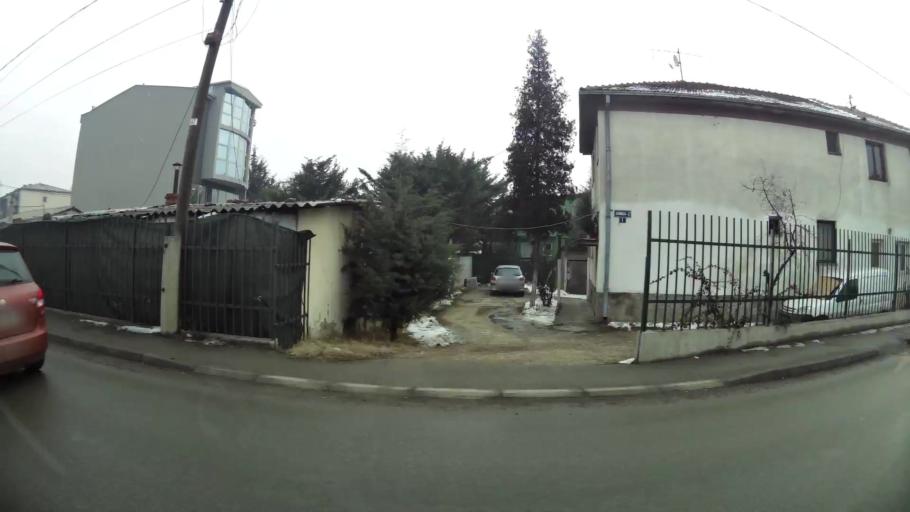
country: MK
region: Kisela Voda
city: Kisela Voda
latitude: 41.9972
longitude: 21.4940
